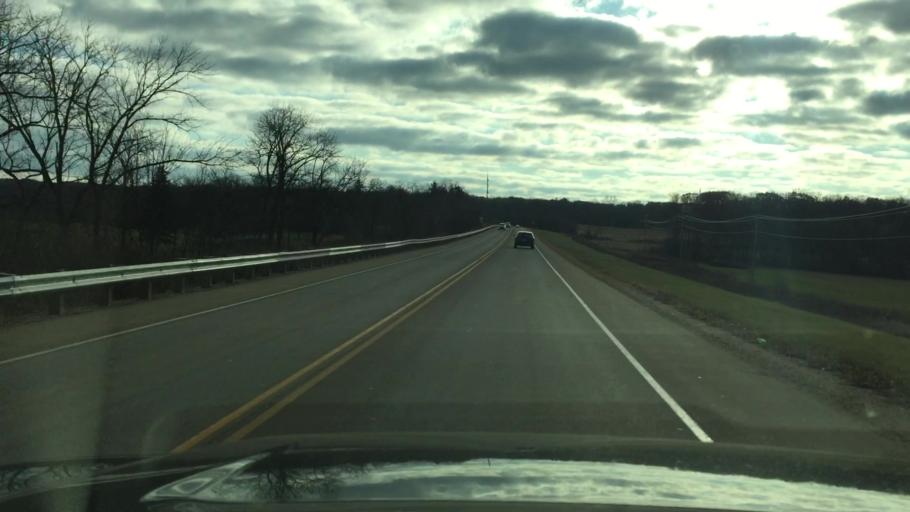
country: US
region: Wisconsin
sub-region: Walworth County
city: Williams Bay
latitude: 42.5863
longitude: -88.5289
